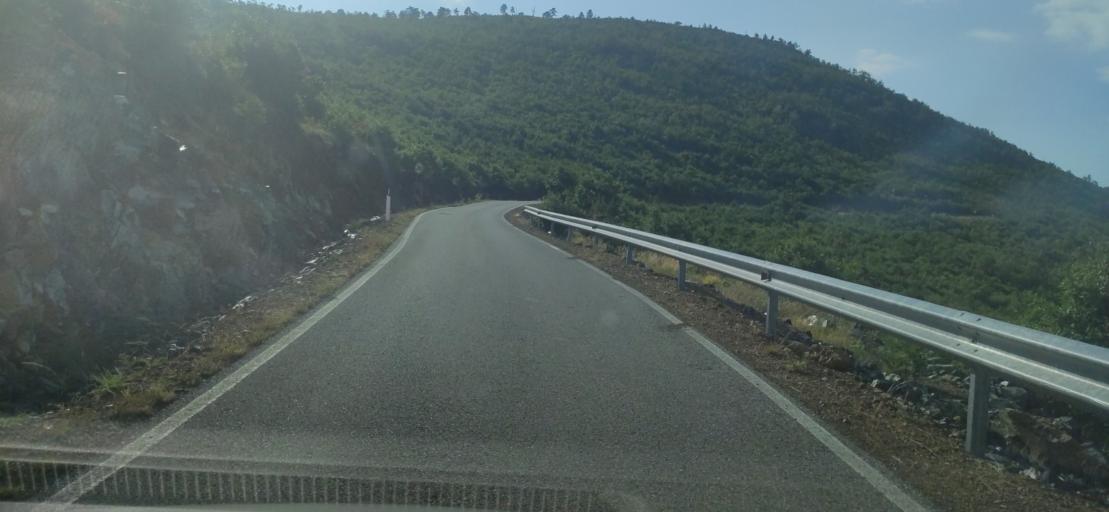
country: AL
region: Shkoder
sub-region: Rrethi i Pukes
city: Iballe
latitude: 42.1713
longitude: 20.0015
